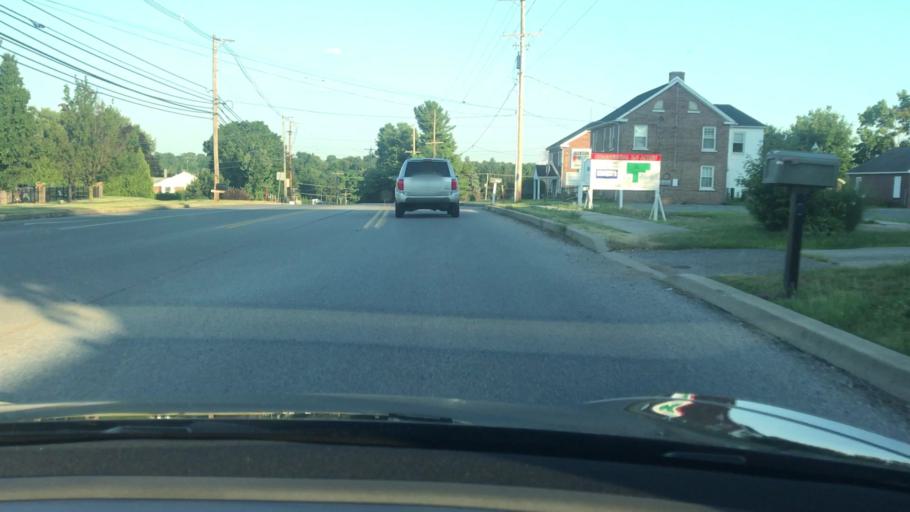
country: US
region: Pennsylvania
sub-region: York County
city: Dover
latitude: 39.9924
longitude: -76.8418
